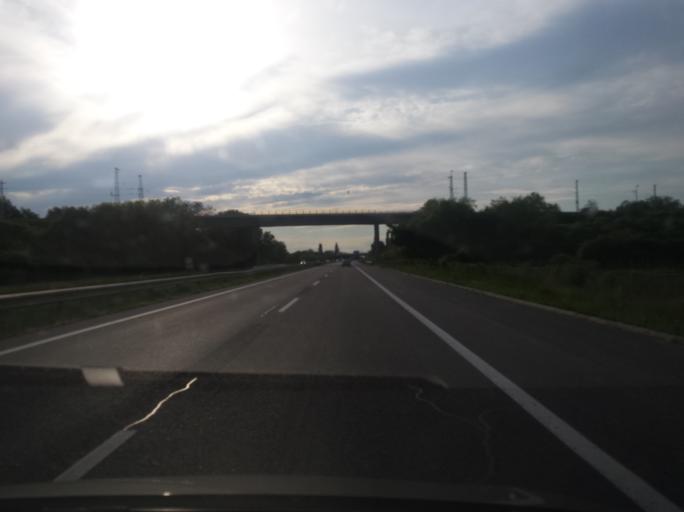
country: AT
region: Burgenland
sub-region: Eisenstadt-Umgebung
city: Mullendorf
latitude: 47.8296
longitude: 16.4644
